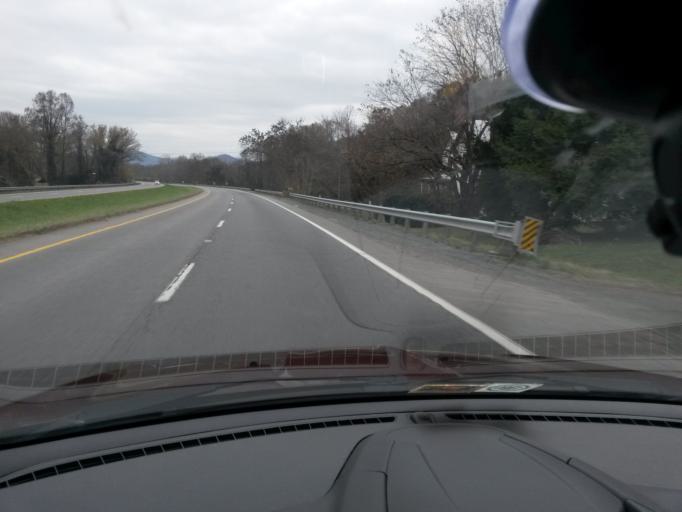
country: US
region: Virginia
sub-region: Nelson County
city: Nellysford
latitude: 37.8868
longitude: -78.7102
